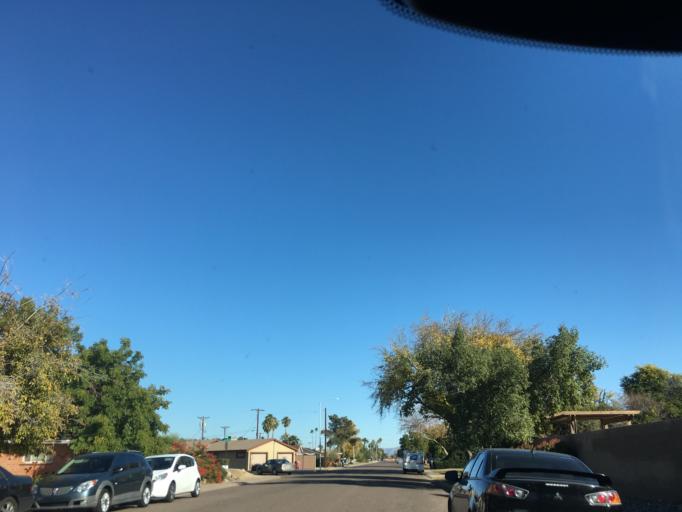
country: US
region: Arizona
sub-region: Maricopa County
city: Scottsdale
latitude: 33.5057
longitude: -111.8990
